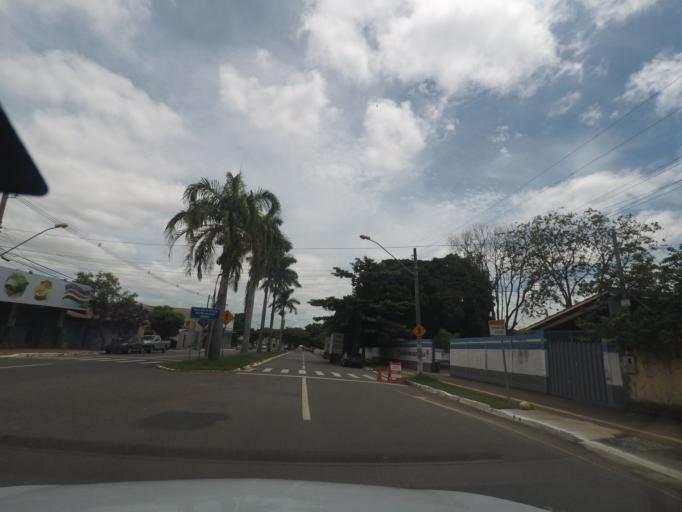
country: BR
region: Goias
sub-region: Goiania
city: Goiania
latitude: -16.6698
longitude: -49.2438
